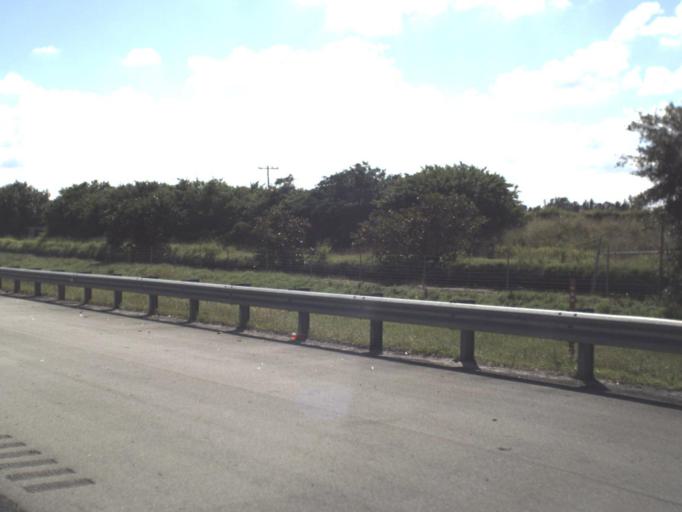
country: US
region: Florida
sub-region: Palm Beach County
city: Villages of Oriole
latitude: 26.4819
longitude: -80.1728
